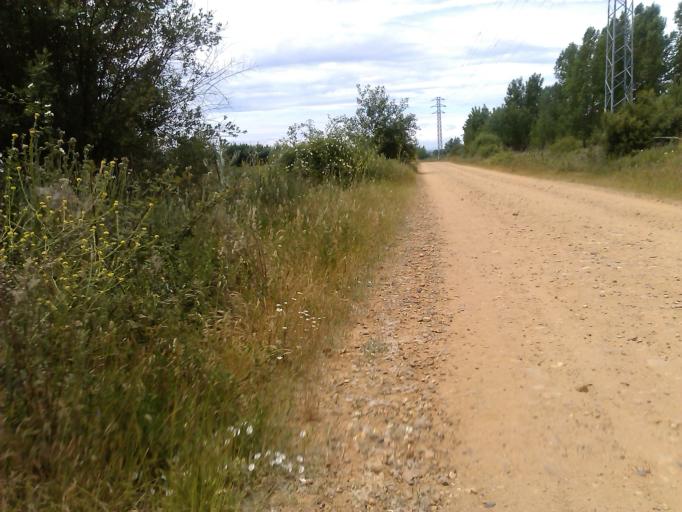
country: ES
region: Castille and Leon
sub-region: Provincia de Leon
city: Bustillo del Paramo
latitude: 42.4598
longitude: -5.7992
